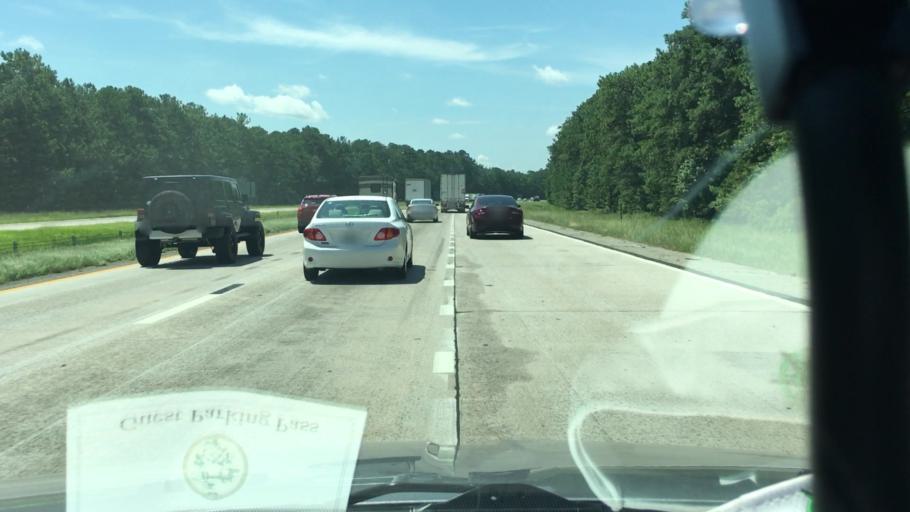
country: US
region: South Carolina
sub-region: Jasper County
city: Hardeeville
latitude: 32.3073
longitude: -81.0601
